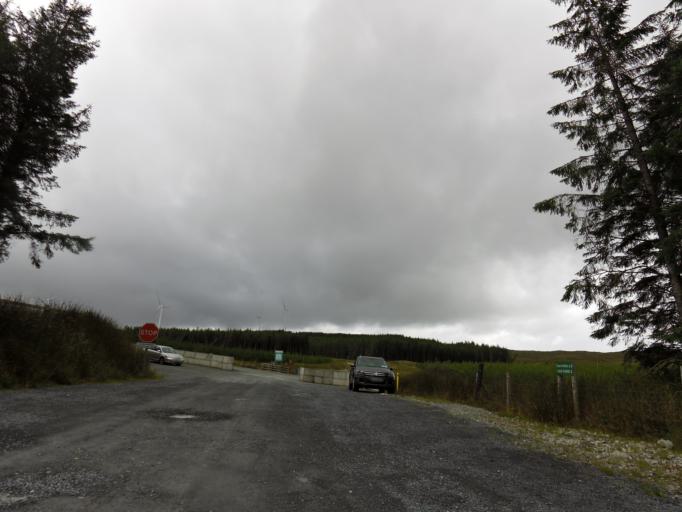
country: IE
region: Connaught
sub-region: County Galway
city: Oughterard
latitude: 53.3826
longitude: -9.3741
